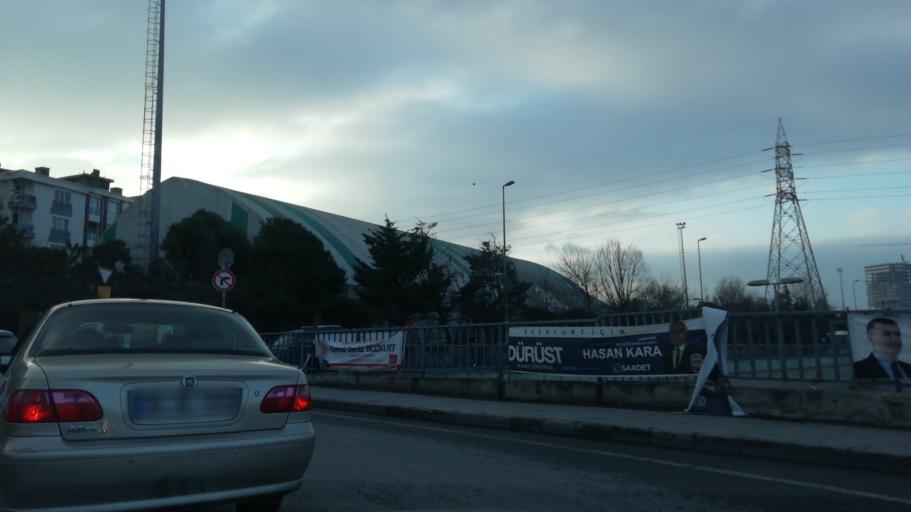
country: TR
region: Istanbul
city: Esenyurt
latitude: 41.0151
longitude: 28.6921
